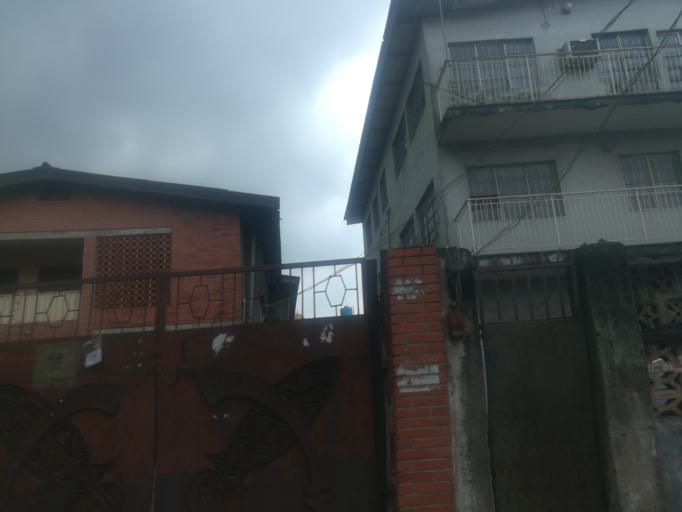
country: NG
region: Lagos
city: Ojota
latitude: 6.5915
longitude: 3.3865
